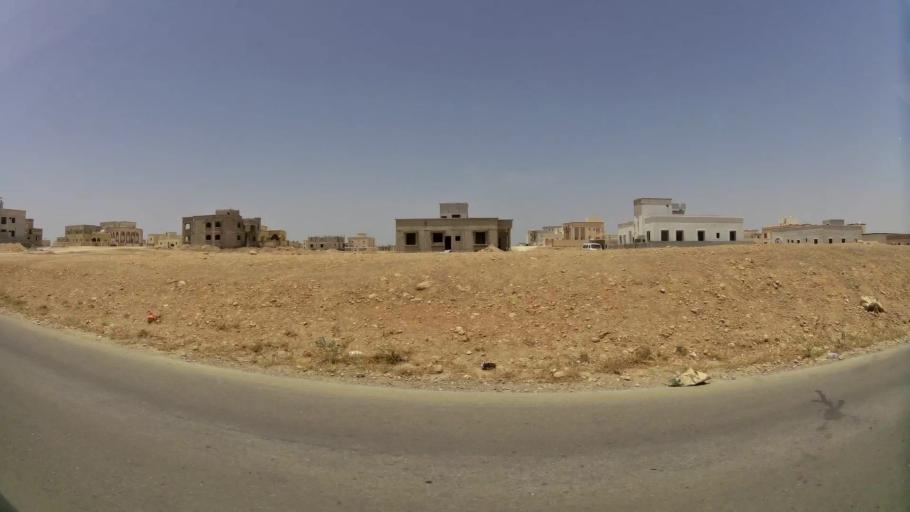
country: OM
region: Zufar
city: Salalah
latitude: 17.0917
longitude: 54.2005
